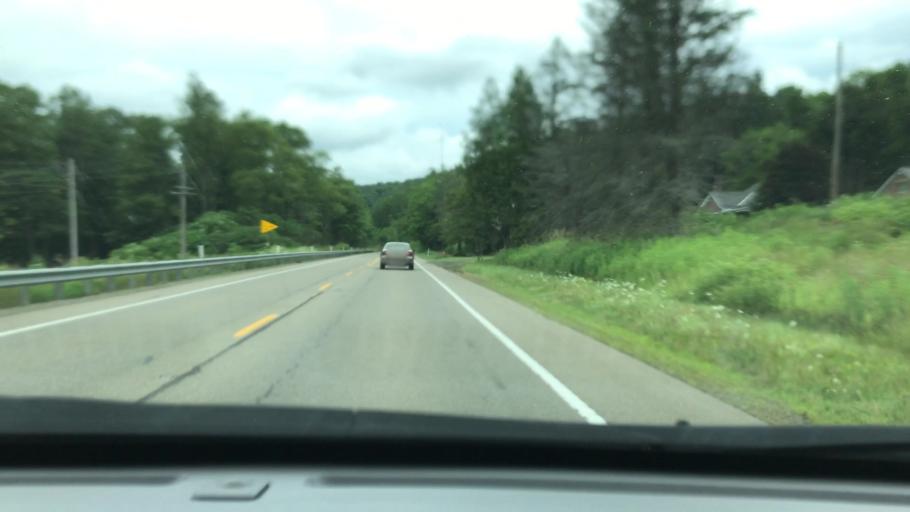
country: US
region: Pennsylvania
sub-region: Elk County
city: Johnsonburg
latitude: 41.5530
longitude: -78.6833
